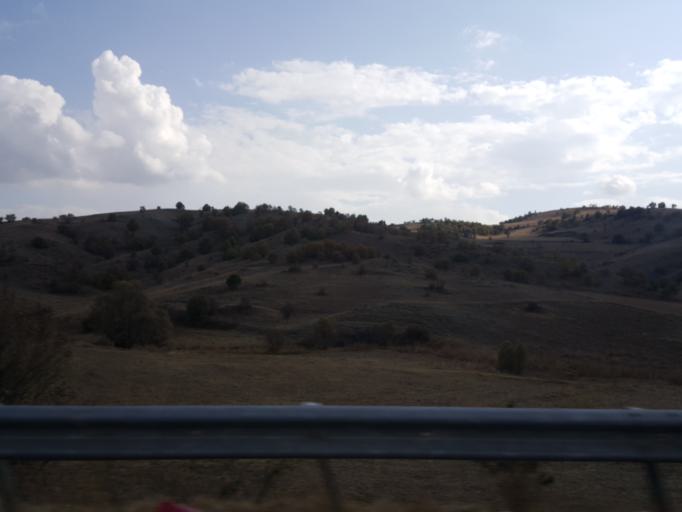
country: TR
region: Corum
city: Alaca
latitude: 40.3144
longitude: 34.6681
